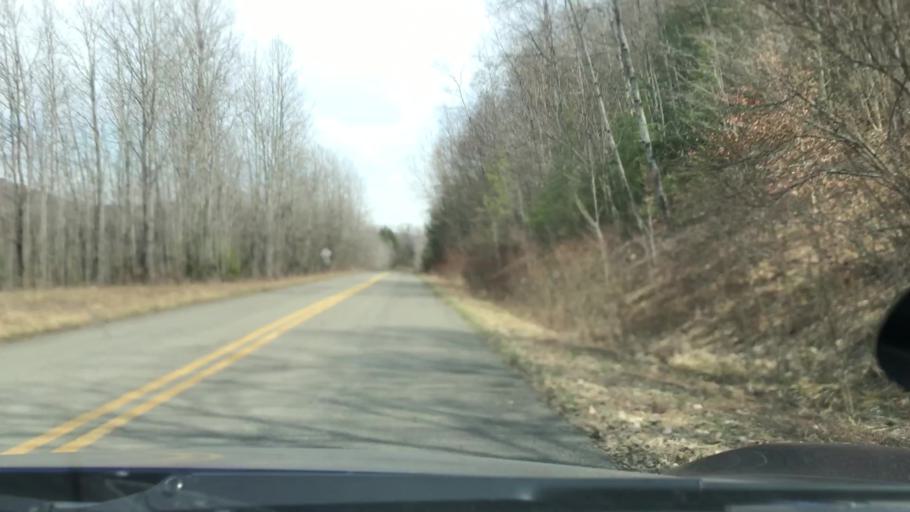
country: US
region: Pennsylvania
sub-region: Warren County
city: Sheffield
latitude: 41.8096
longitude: -78.9348
